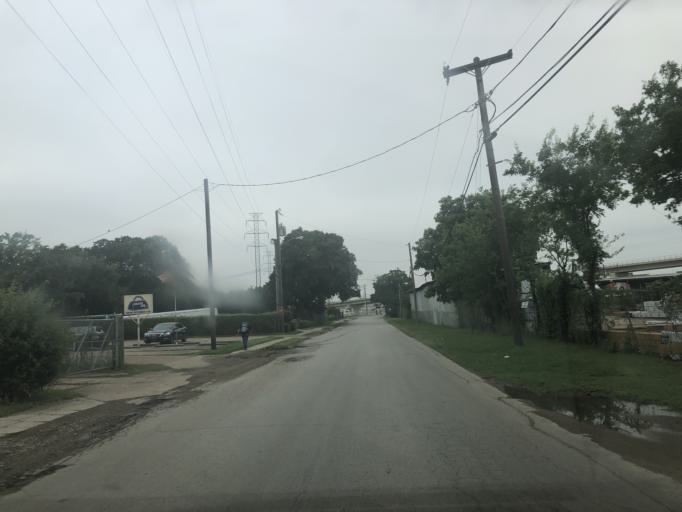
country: US
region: Texas
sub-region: Dallas County
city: Farmers Branch
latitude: 32.8610
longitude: -96.8765
